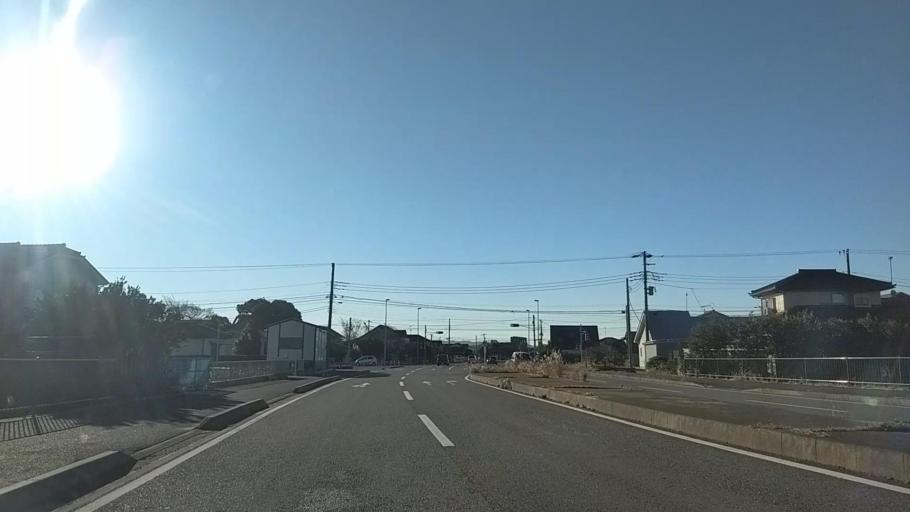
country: JP
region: Chiba
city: Kisarazu
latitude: 35.4004
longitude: 139.9207
